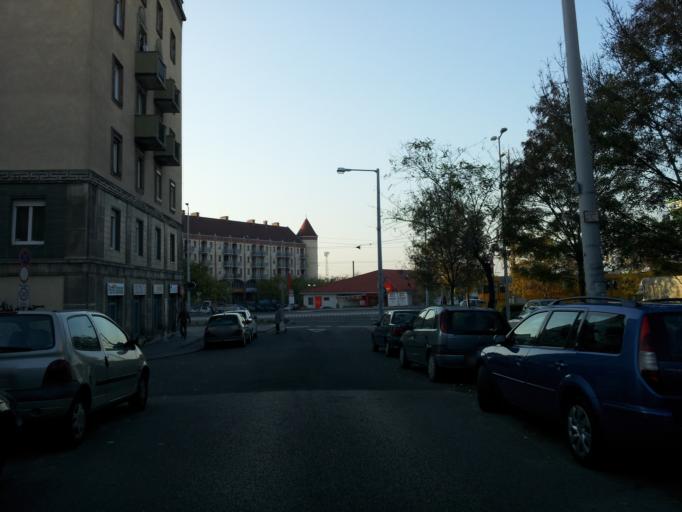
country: HU
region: Budapest
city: Budapest X. keruelet
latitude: 47.4903
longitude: 19.1383
